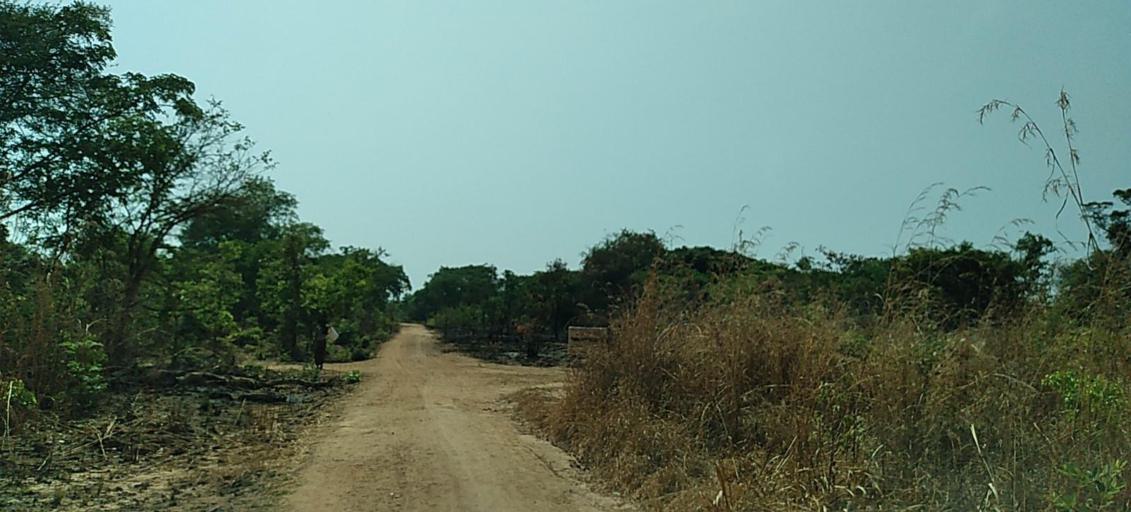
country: ZM
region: Copperbelt
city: Luanshya
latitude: -13.2811
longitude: 28.3161
